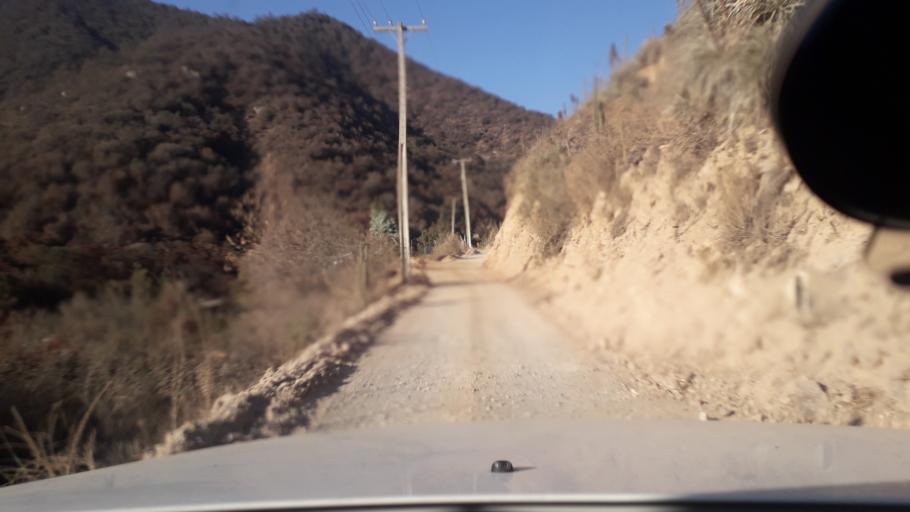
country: CL
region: Valparaiso
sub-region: Provincia de Marga Marga
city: Limache
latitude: -33.0523
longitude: -71.0794
